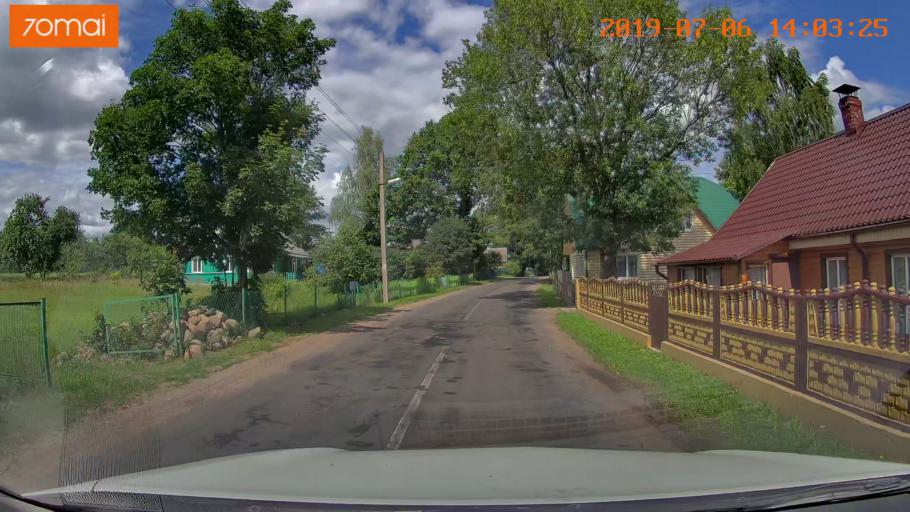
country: BY
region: Minsk
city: Ivyanyets
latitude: 53.8306
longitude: 26.8000
